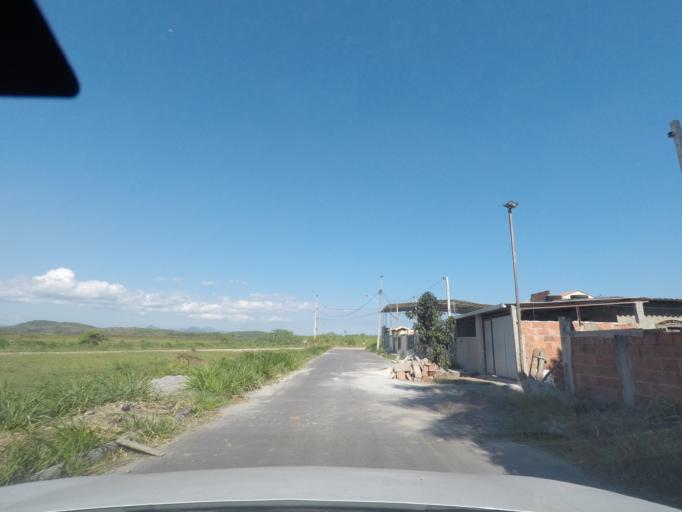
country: BR
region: Rio de Janeiro
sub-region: Marica
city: Marica
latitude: -22.9647
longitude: -42.9214
